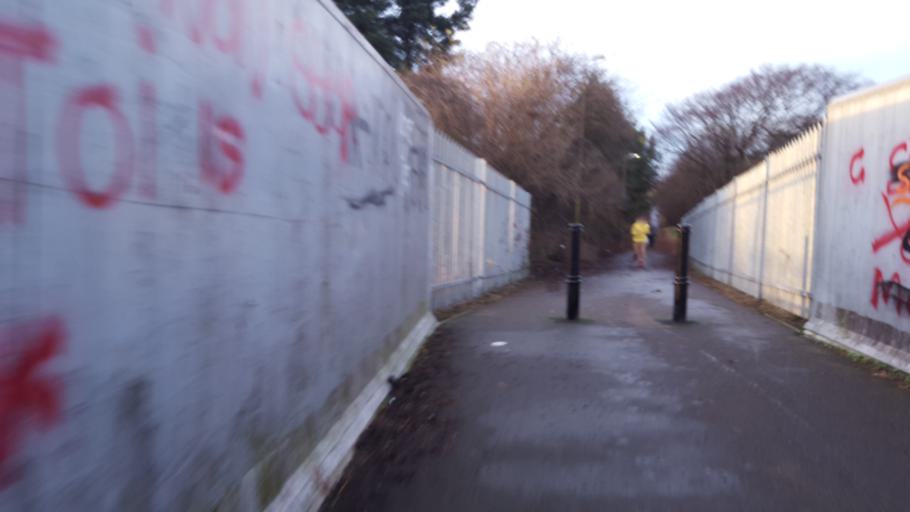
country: GB
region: Scotland
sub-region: West Lothian
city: Livingston
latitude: 55.9125
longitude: -3.5261
